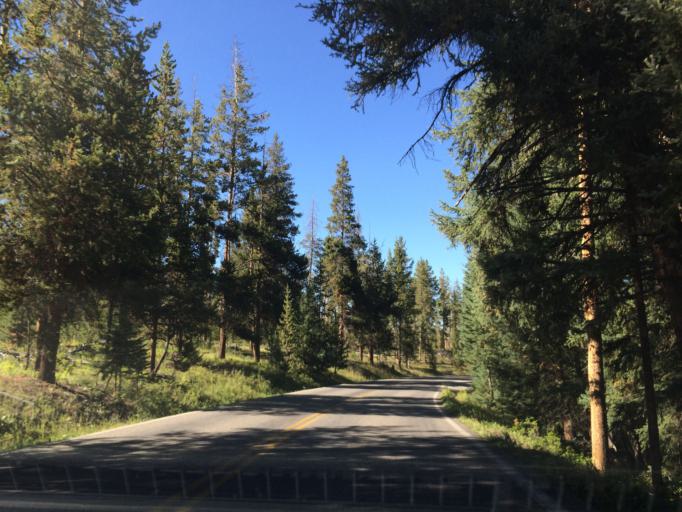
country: US
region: Montana
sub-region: Gallatin County
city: West Yellowstone
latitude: 44.8775
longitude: -110.3814
